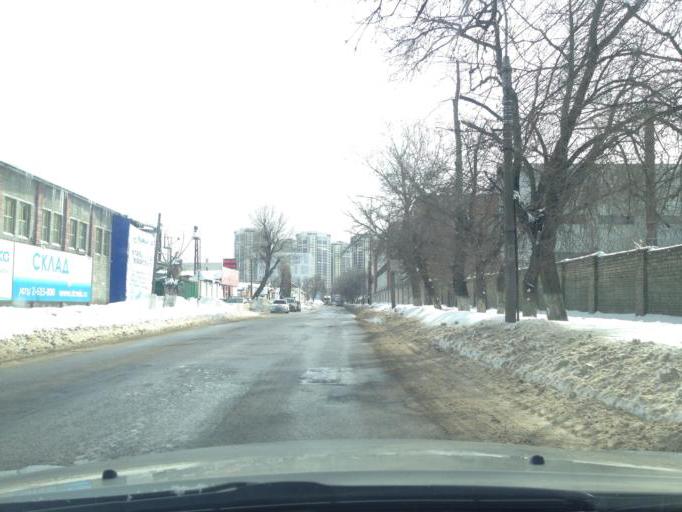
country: RU
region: Voronezj
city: Voronezh
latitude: 51.6603
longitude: 39.1739
